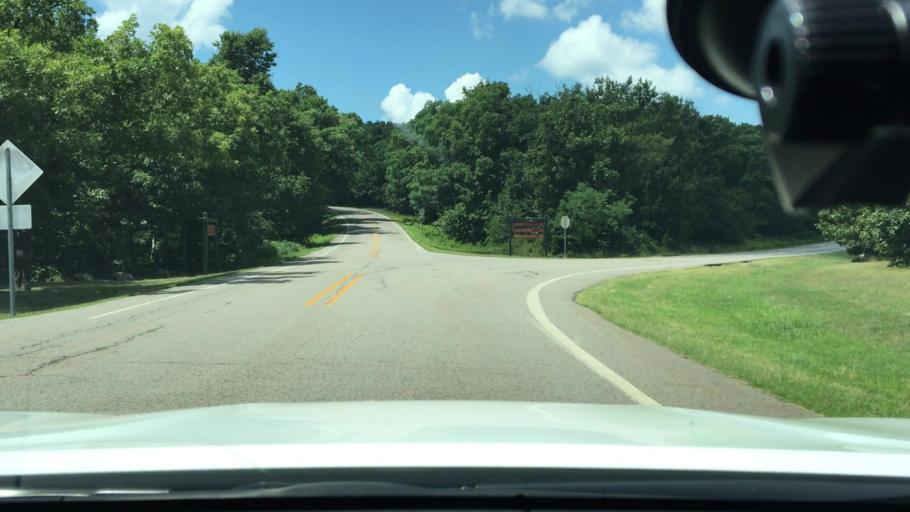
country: US
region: Arkansas
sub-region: Logan County
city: Paris
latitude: 35.1743
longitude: -93.6184
